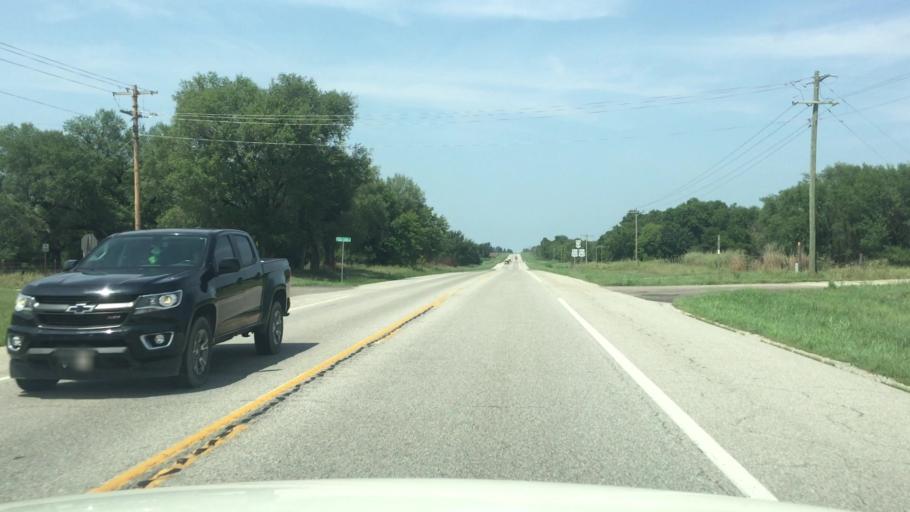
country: US
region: Missouri
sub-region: Jasper County
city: Carl Junction
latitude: 37.2510
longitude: -94.7051
